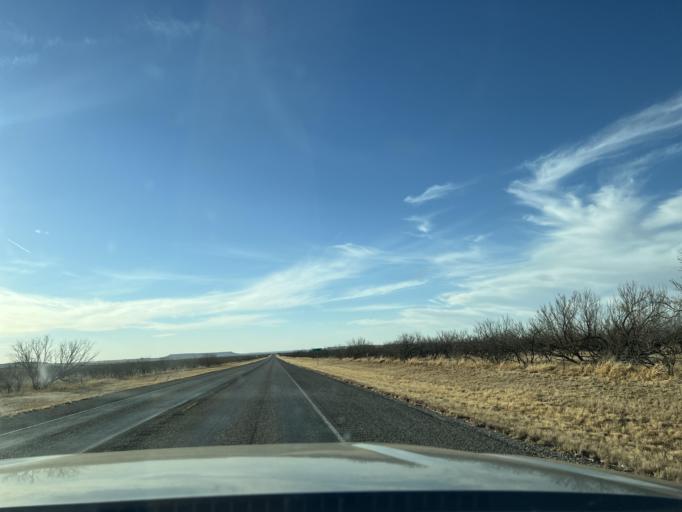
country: US
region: Texas
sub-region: Borden County
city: Gail
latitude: 32.7664
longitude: -101.2924
